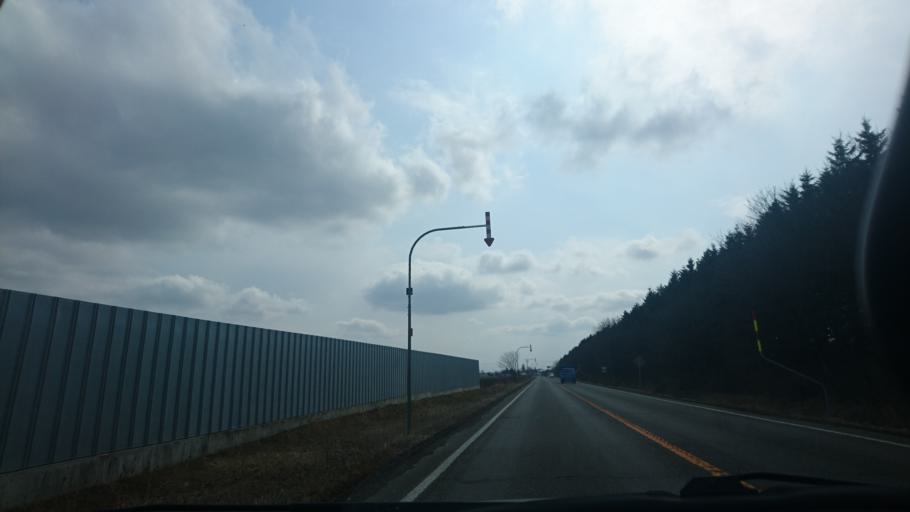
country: JP
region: Hokkaido
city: Otofuke
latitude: 43.1587
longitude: 143.2459
